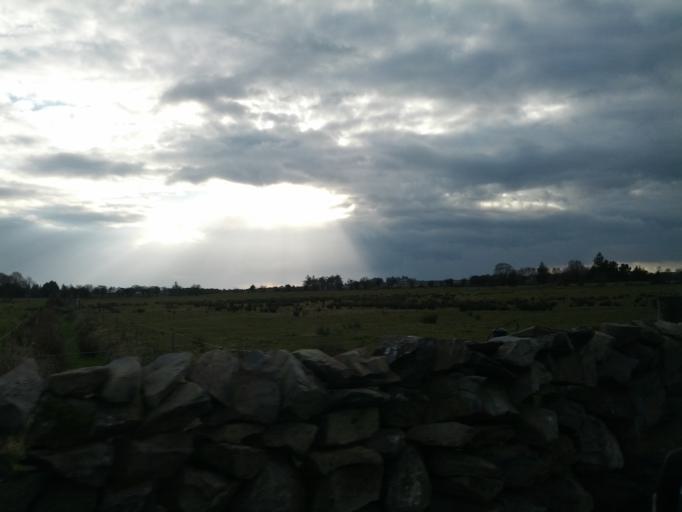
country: IE
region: Connaught
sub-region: County Galway
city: Athenry
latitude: 53.3528
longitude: -8.6690
